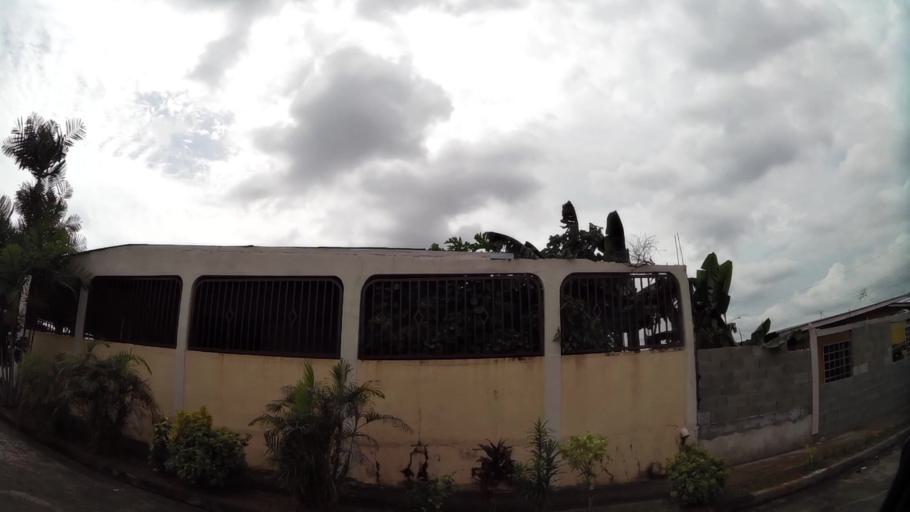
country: PA
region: Panama
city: San Miguelito
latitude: 9.0574
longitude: -79.4228
